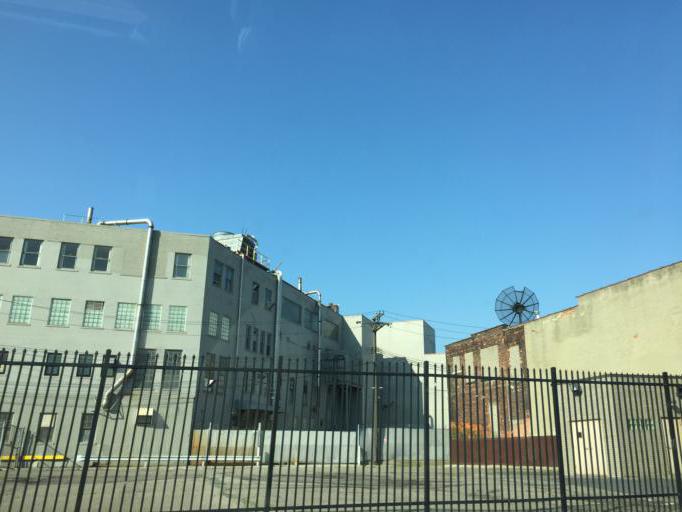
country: US
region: Michigan
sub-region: Wayne County
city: Detroit
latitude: 42.3377
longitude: -83.0623
